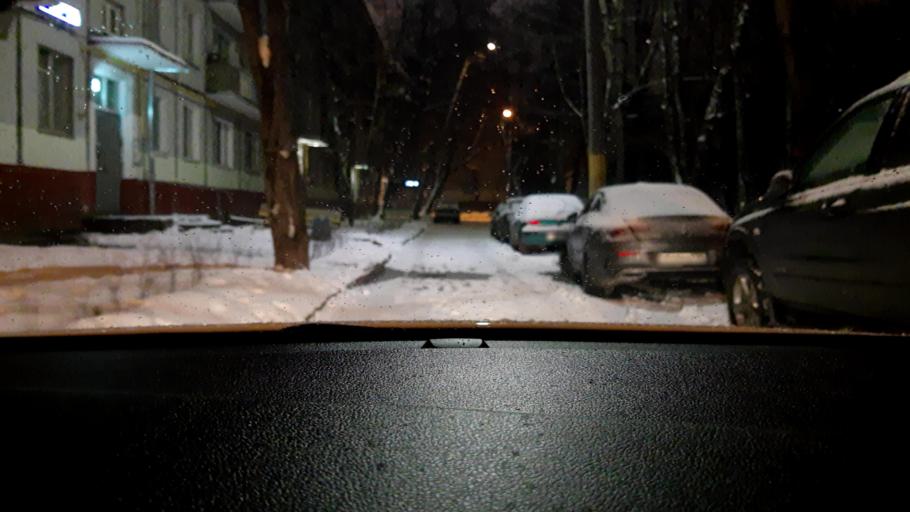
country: RU
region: Moscow
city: Businovo
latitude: 55.8789
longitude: 37.5180
